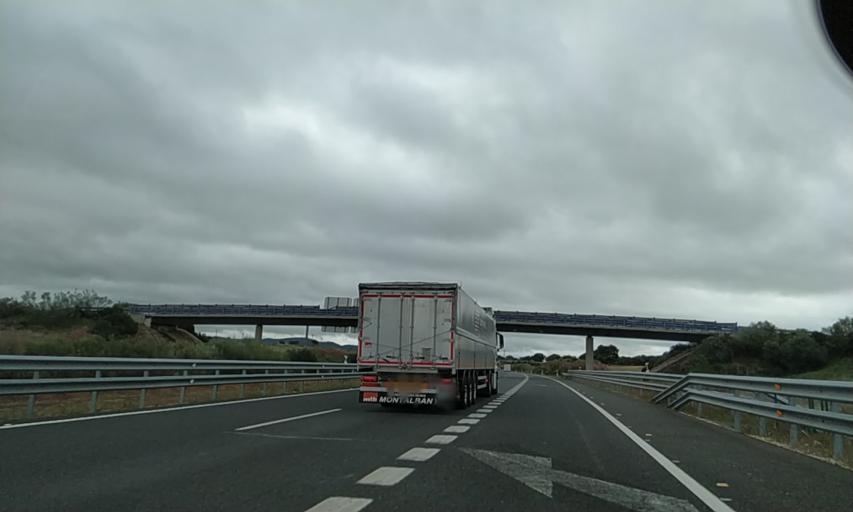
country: ES
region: Extremadura
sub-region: Provincia de Caceres
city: Caceres
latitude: 39.4577
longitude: -6.4204
